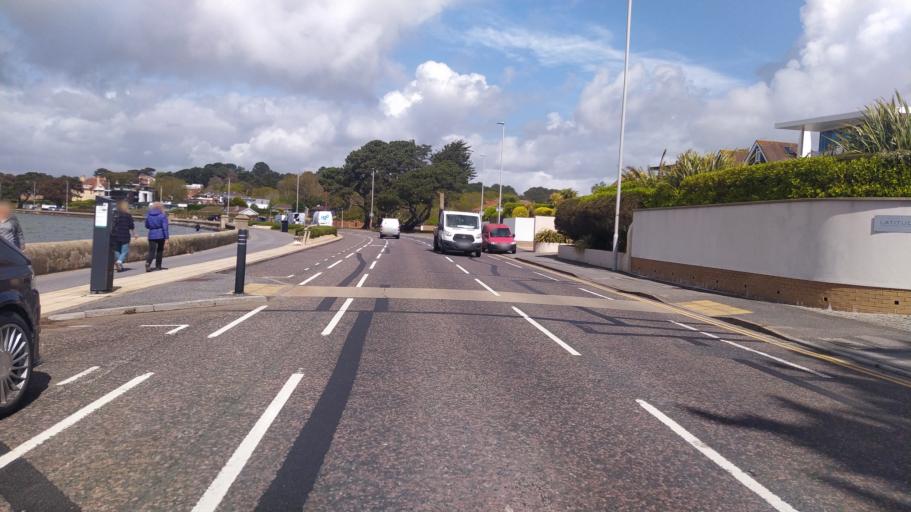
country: GB
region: England
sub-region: Dorset
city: Parkstone
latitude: 50.6997
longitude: -1.9344
